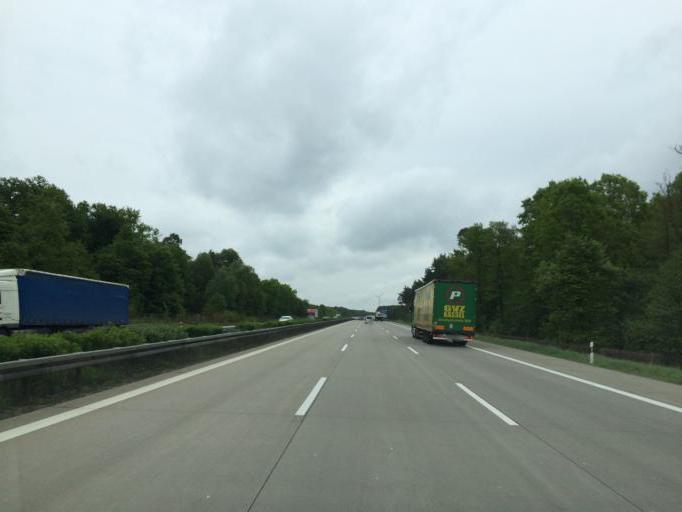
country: DE
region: Saxony-Anhalt
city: Tucheim
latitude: 52.2500
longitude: 12.1946
